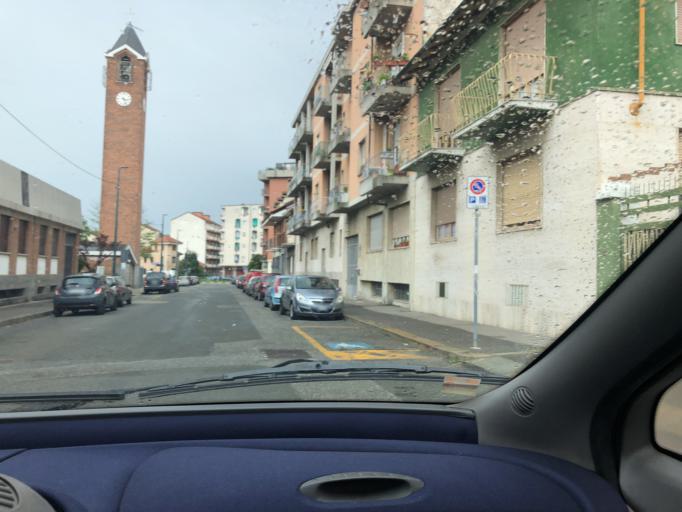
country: IT
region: Piedmont
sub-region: Provincia di Torino
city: Lesna
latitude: 45.0791
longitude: 7.6197
